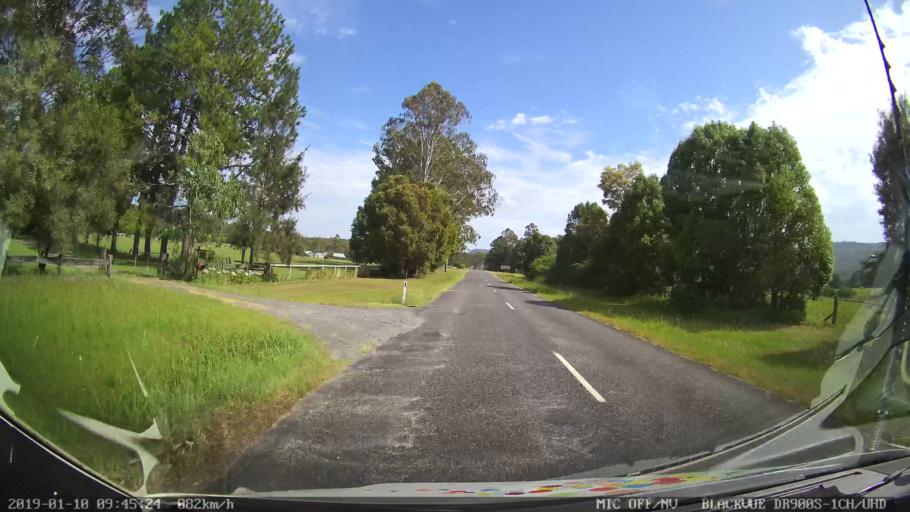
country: AU
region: New South Wales
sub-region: Coffs Harbour
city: Nana Glen
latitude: -30.1051
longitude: 153.0039
